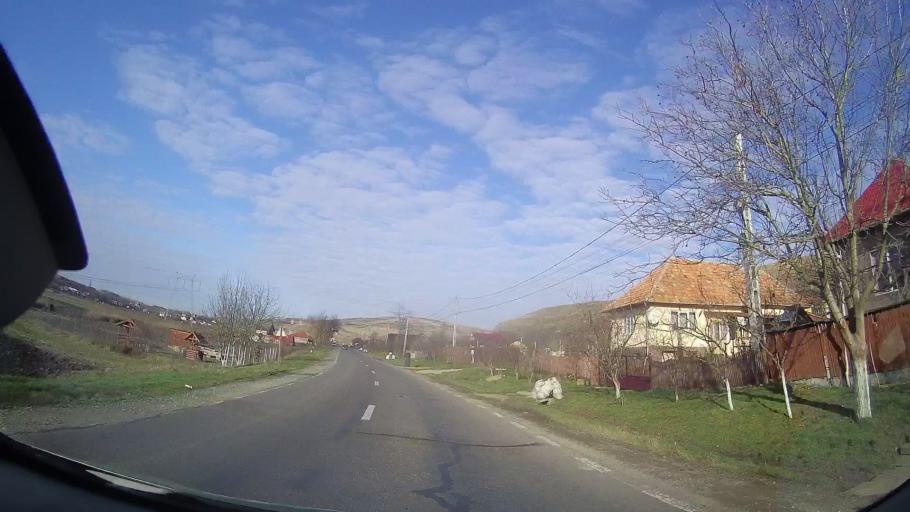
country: RO
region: Cluj
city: Caianu Mic
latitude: 46.8048
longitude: 23.8737
